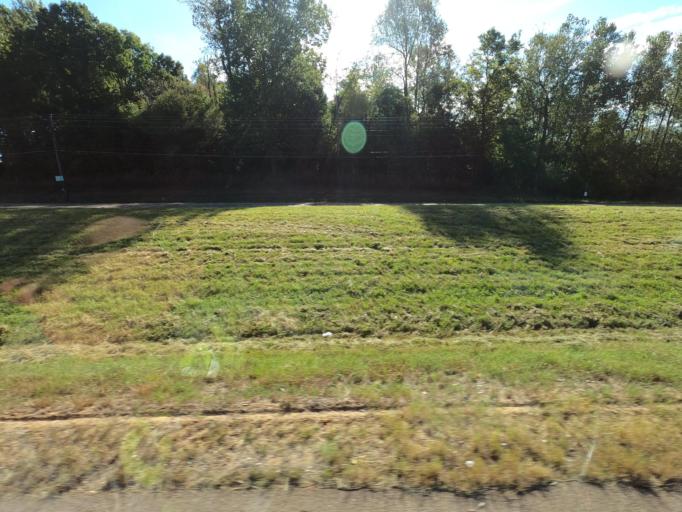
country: US
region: Tennessee
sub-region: Tipton County
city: Munford
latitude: 35.4277
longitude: -89.8106
